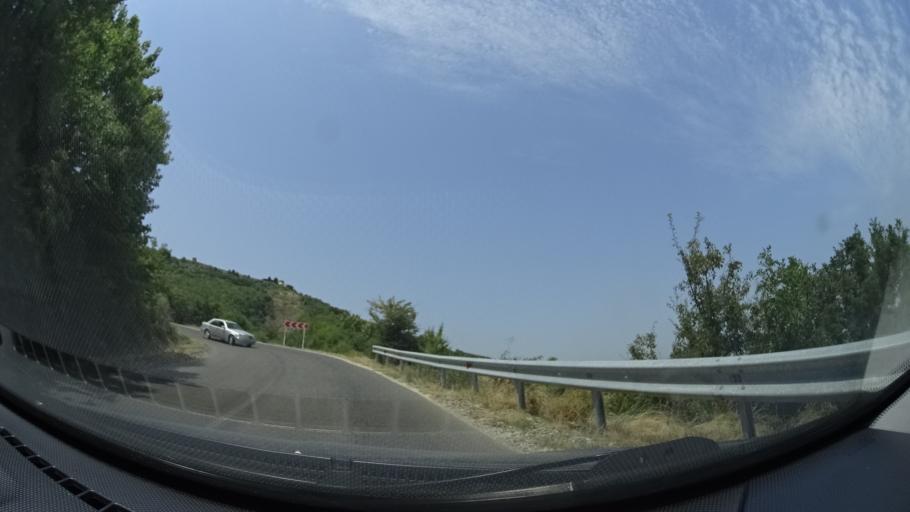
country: GE
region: Kakheti
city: Sighnaghi
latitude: 41.6241
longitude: 45.9310
